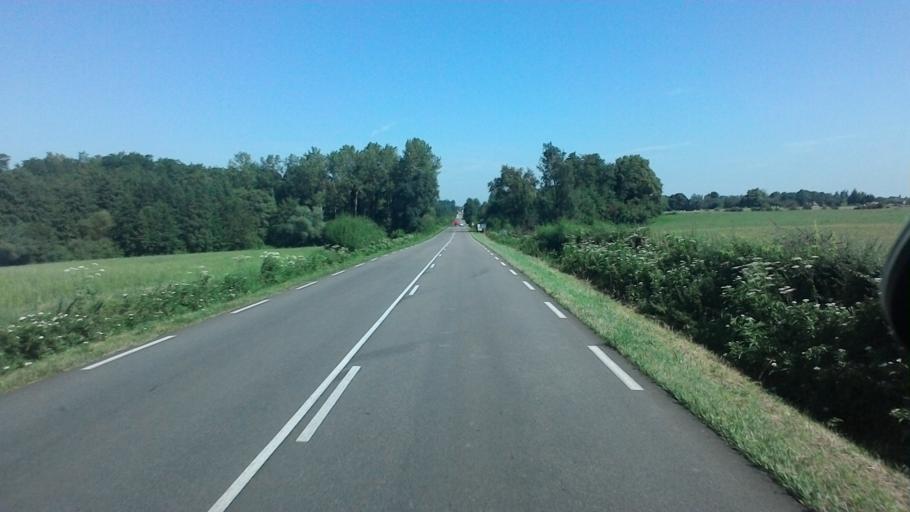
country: FR
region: Bourgogne
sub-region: Departement de Saone-et-Loire
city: Romenay
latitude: 46.4881
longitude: 5.0708
